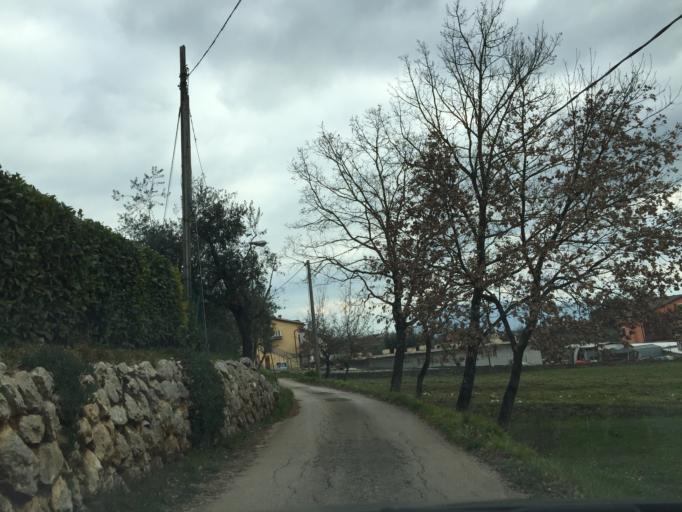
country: IT
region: Latium
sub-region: Provincia di Frosinone
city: Cassino
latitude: 41.4828
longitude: 13.8019
